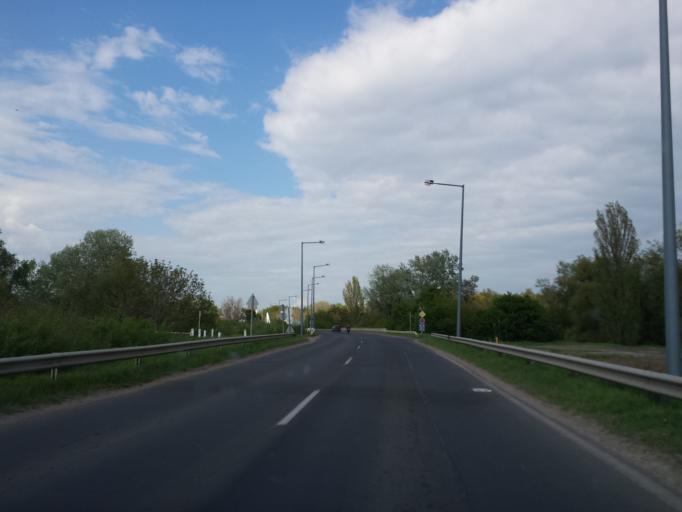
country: HU
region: Csongrad
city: Kiszombor
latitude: 46.2001
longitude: 20.4512
